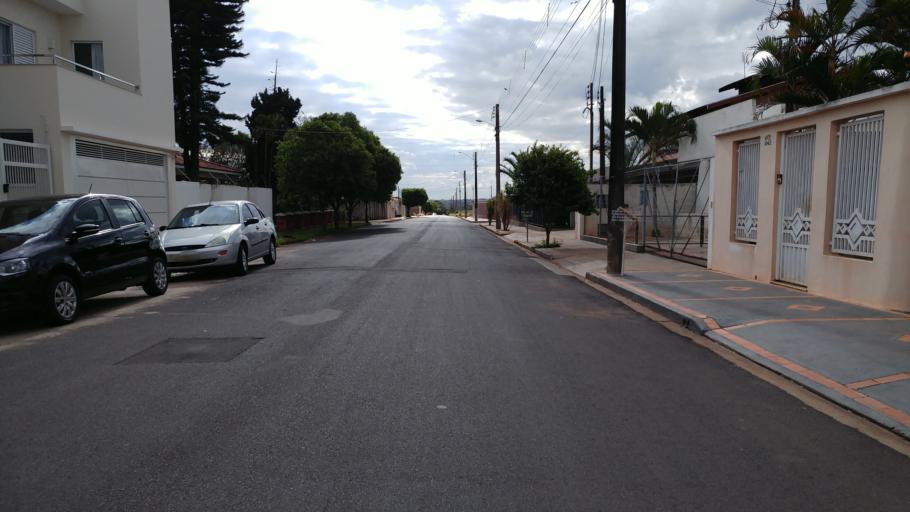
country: BR
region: Sao Paulo
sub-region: Paraguacu Paulista
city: Paraguacu Paulista
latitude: -22.4105
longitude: -50.5829
